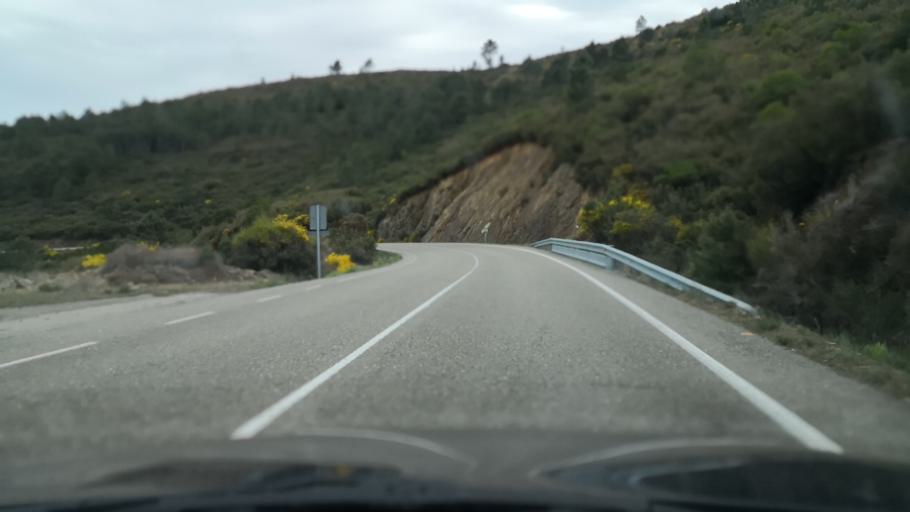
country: ES
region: Extremadura
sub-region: Provincia de Caceres
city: Acebo
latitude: 40.2329
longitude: -6.6858
